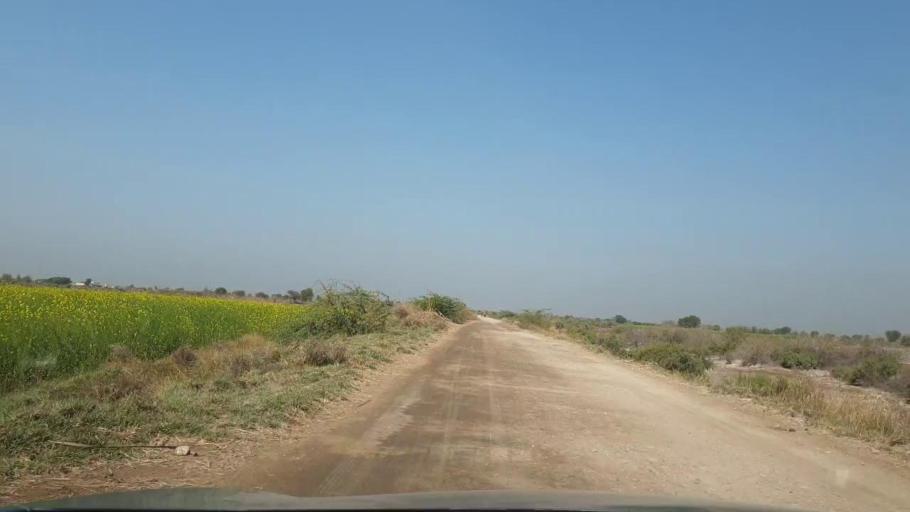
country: PK
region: Sindh
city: Berani
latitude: 25.7174
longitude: 68.8553
